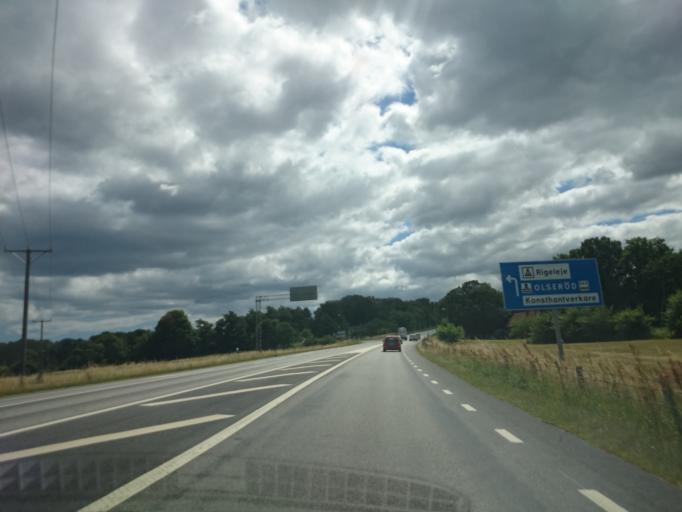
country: SE
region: Skane
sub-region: Kristianstads Kommun
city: Degeberga
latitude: 55.8055
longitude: 14.1461
